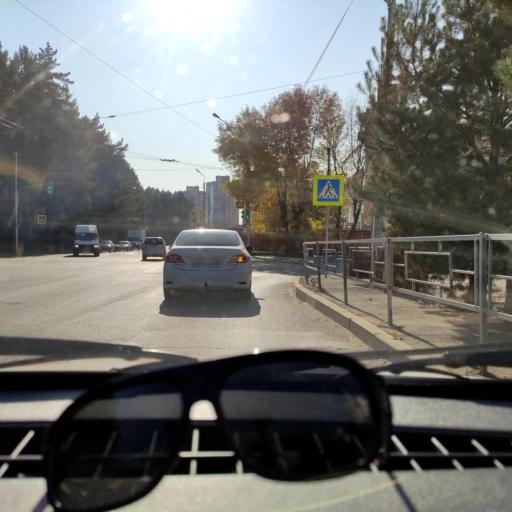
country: RU
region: Bashkortostan
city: Ufa
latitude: 54.6932
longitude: 56.0024
